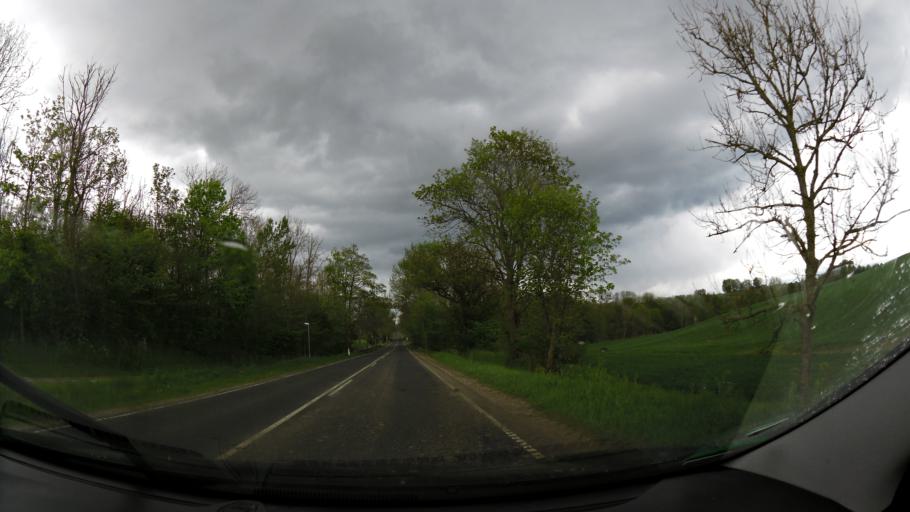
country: DK
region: South Denmark
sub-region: Nyborg Kommune
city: Nyborg
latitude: 55.2277
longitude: 10.7356
